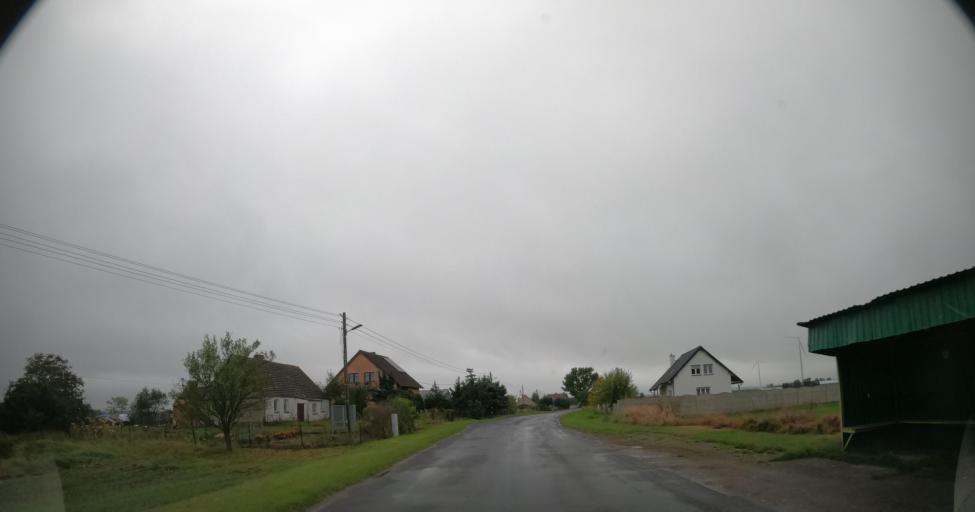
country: PL
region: West Pomeranian Voivodeship
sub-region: Powiat pyrzycki
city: Kozielice
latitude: 53.0699
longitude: 14.7872
